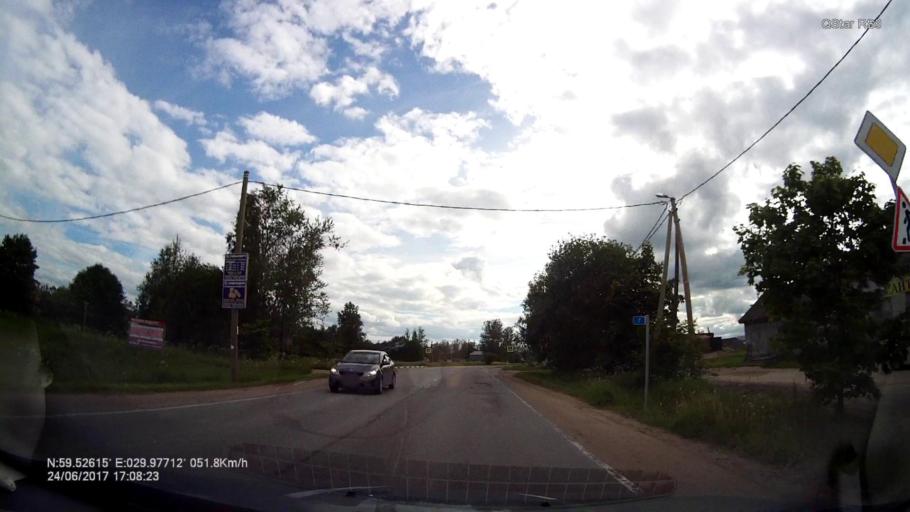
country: RU
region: Leningrad
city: Voyskovitsy
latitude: 59.5259
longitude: 29.9768
